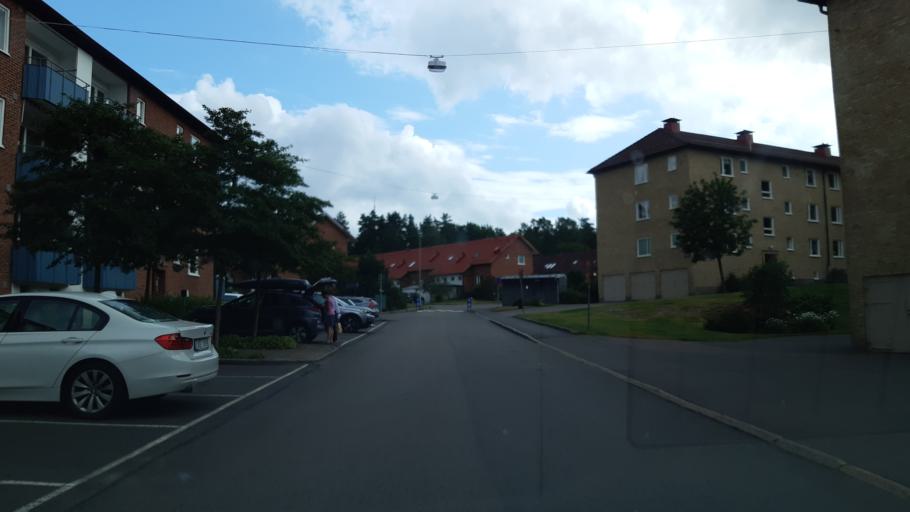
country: SE
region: Vaestra Goetaland
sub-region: Partille Kommun
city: Partille
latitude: 57.7140
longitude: 12.0544
